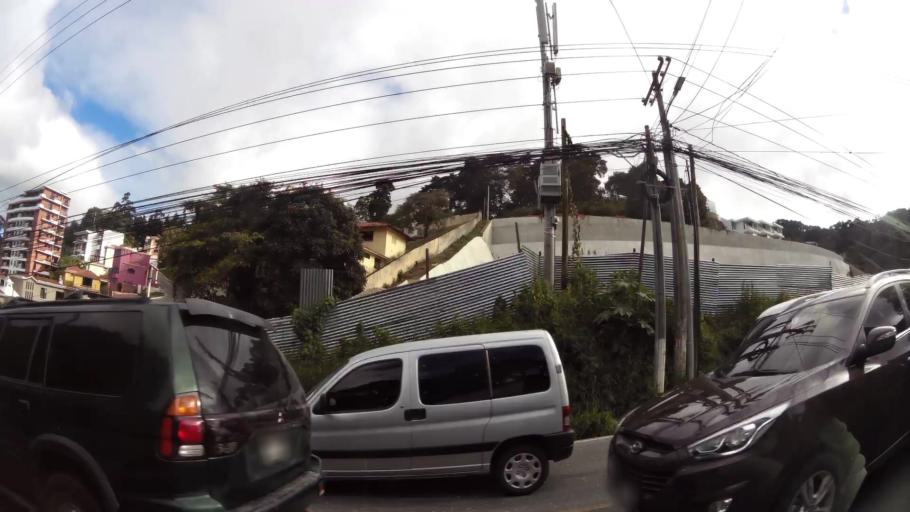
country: GT
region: Guatemala
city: Santa Catarina Pinula
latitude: 14.5698
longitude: -90.4861
